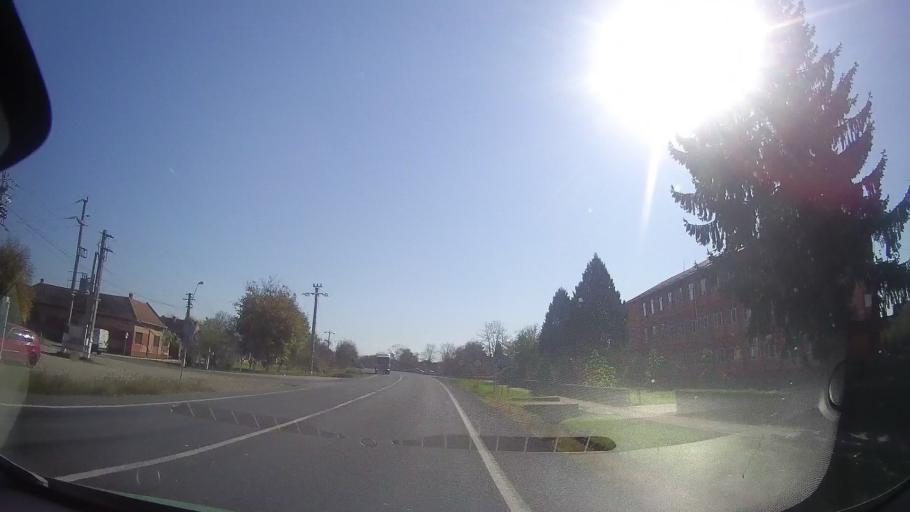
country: RO
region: Timis
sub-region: Comuna Belint
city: Belint
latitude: 45.7502
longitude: 21.7650
